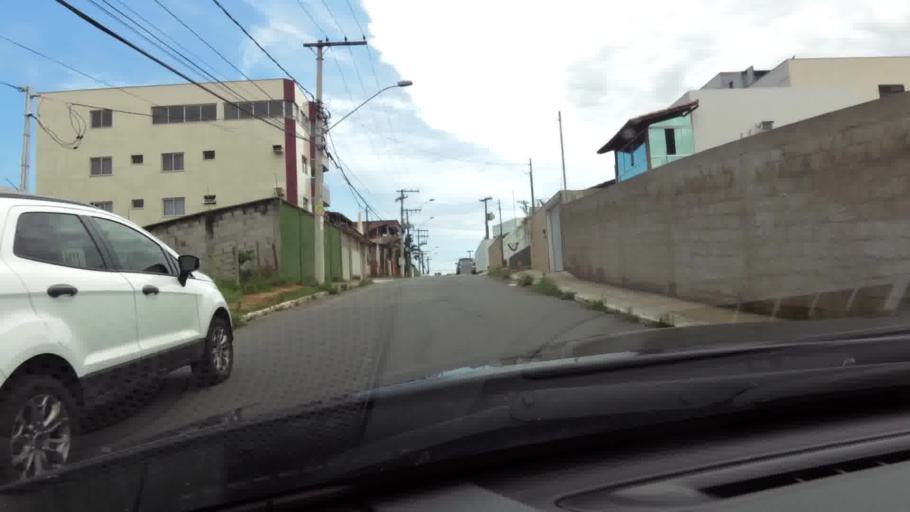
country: BR
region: Espirito Santo
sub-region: Guarapari
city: Guarapari
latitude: -20.6535
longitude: -40.5023
